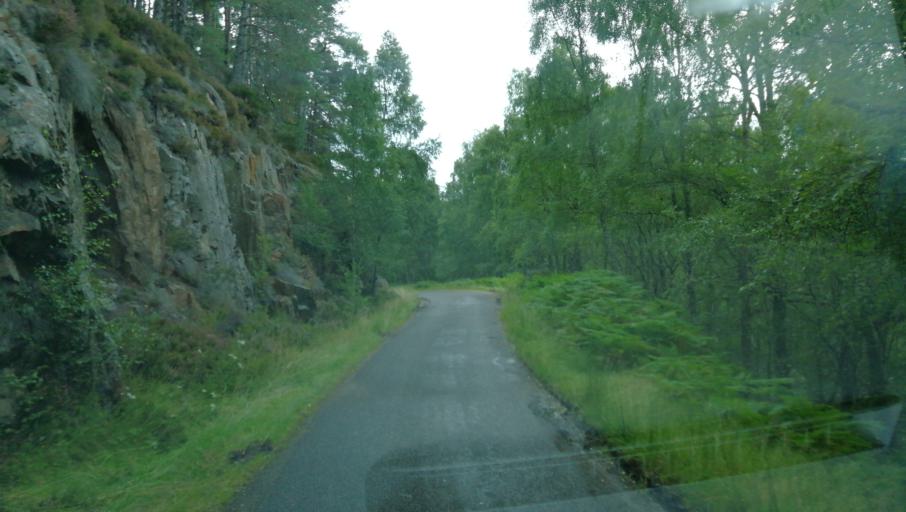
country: GB
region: Scotland
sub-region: Highland
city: Spean Bridge
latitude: 57.2968
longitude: -4.9052
